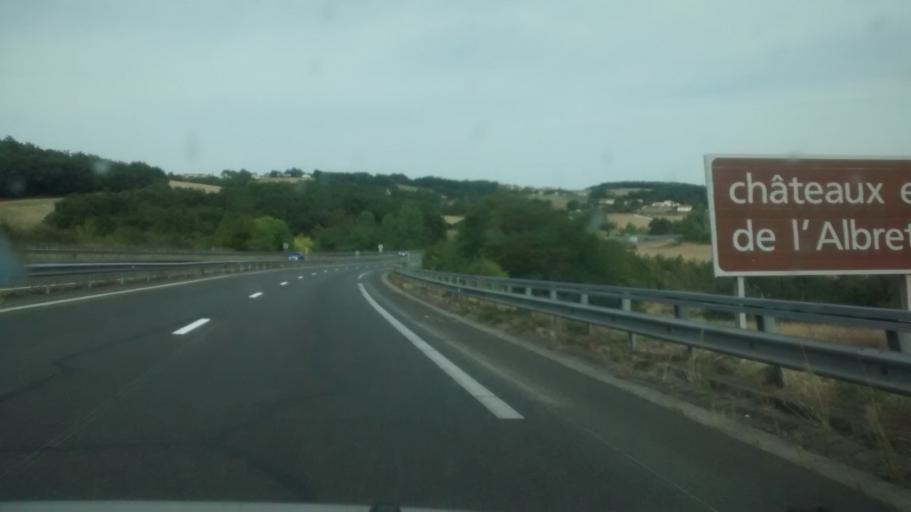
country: FR
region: Aquitaine
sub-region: Departement du Lot-et-Garonne
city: Boe
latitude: 44.1465
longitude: 0.6257
